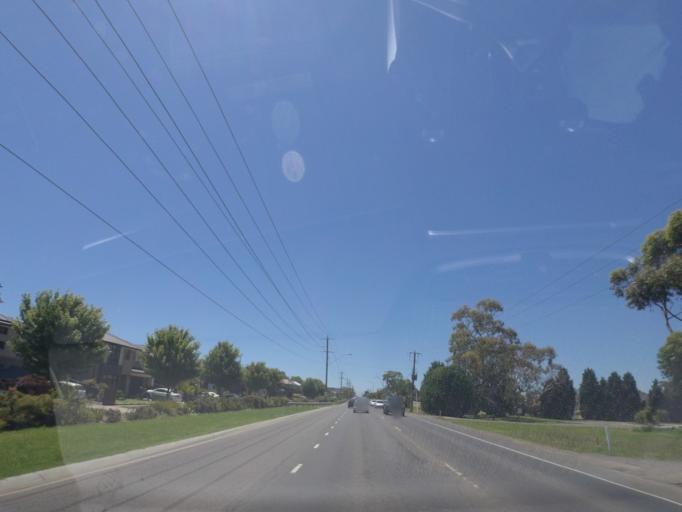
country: AU
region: Victoria
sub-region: Whittlesea
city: Epping
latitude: -37.6328
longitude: 145.0271
